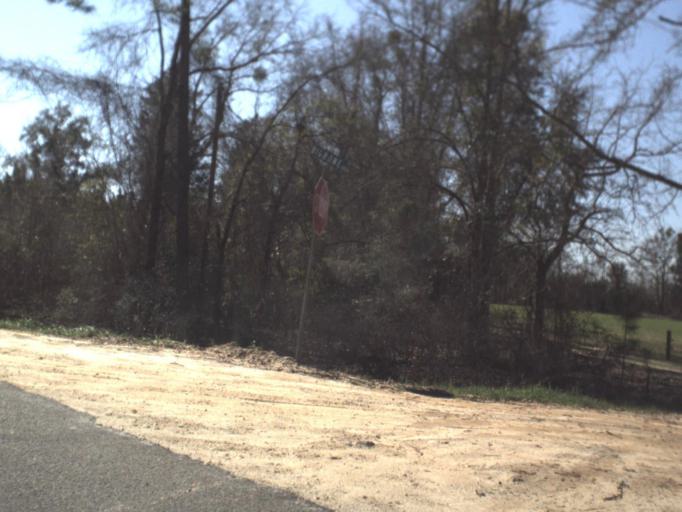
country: US
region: Florida
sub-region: Jackson County
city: Marianna
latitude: 30.6090
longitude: -85.1473
